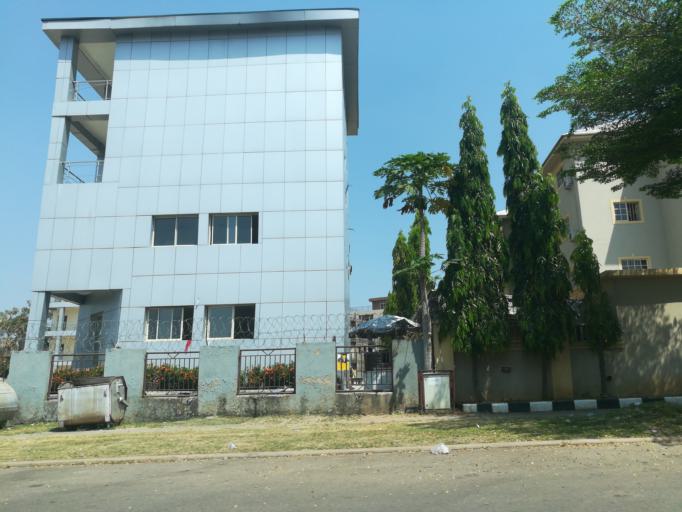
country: NG
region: Abuja Federal Capital Territory
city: Abuja
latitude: 9.0710
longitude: 7.4263
